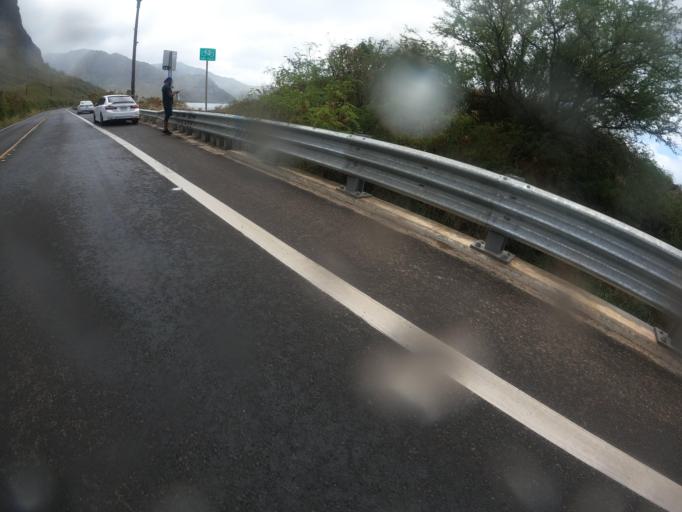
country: US
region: Hawaii
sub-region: Honolulu County
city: Makaha Valley
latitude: 21.5451
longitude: -158.2396
